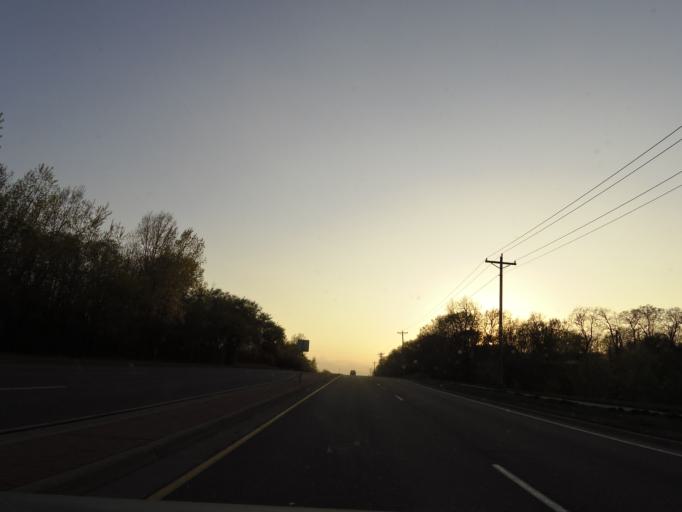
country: US
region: Minnesota
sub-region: Scott County
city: Prior Lake
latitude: 44.7466
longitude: -93.3975
